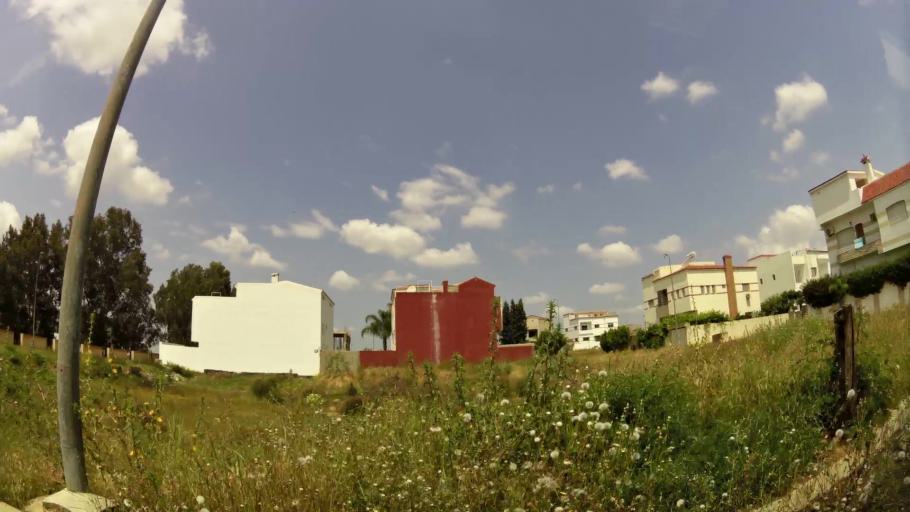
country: MA
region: Gharb-Chrarda-Beni Hssen
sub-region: Kenitra Province
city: Kenitra
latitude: 34.0128
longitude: -6.5363
